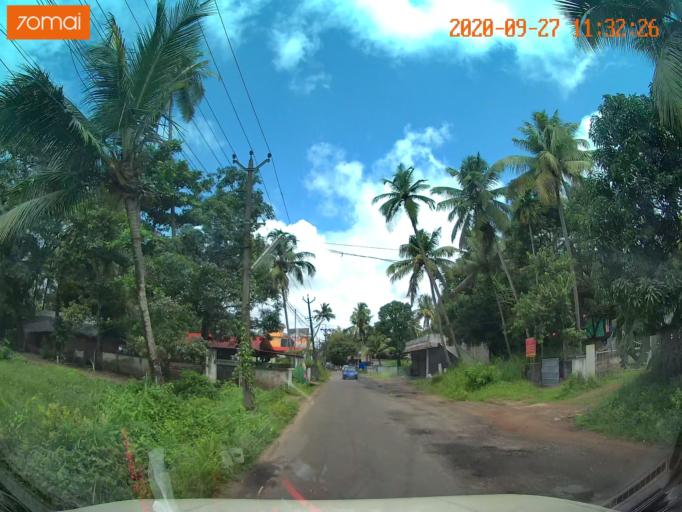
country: IN
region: Kerala
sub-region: Thrissur District
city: Thanniyam
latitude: 10.4273
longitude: 76.1306
